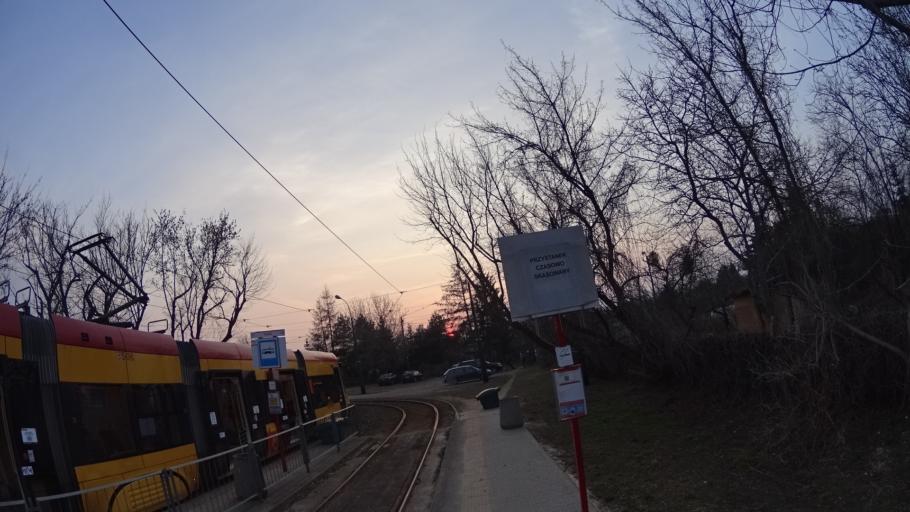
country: PL
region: Masovian Voivodeship
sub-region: Warszawa
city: Bemowo
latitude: 52.2473
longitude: 20.9382
